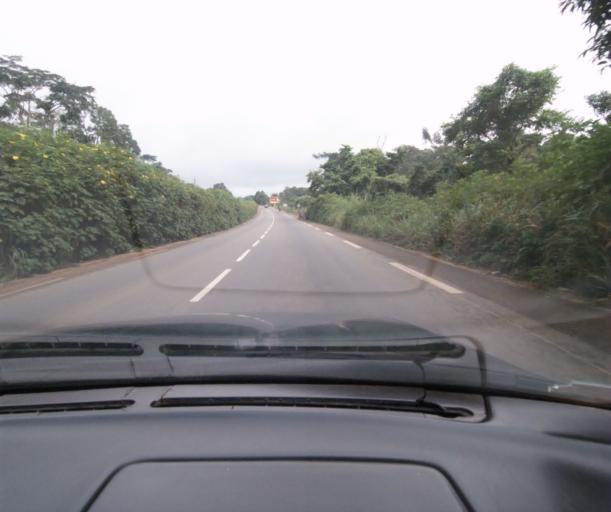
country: CM
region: Centre
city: Obala
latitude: 4.1612
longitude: 11.5051
